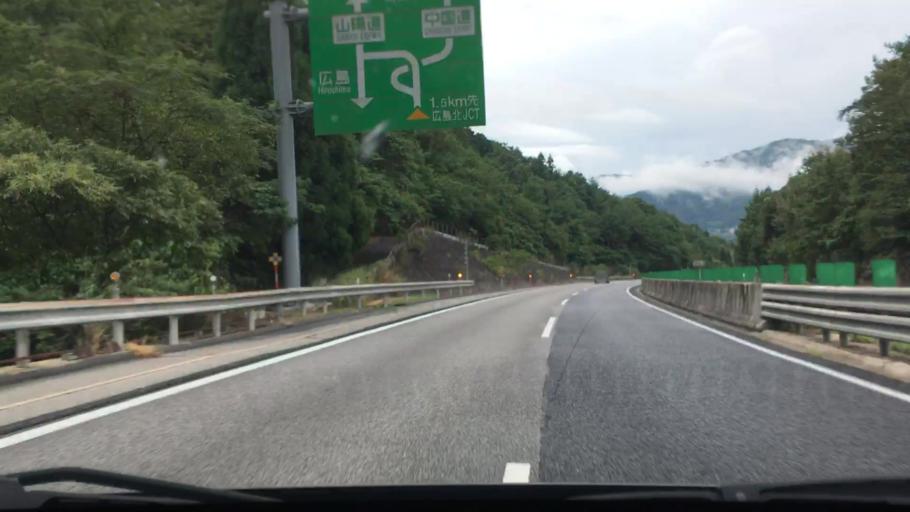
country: JP
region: Hiroshima
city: Hiroshima-shi
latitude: 34.5834
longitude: 132.4730
